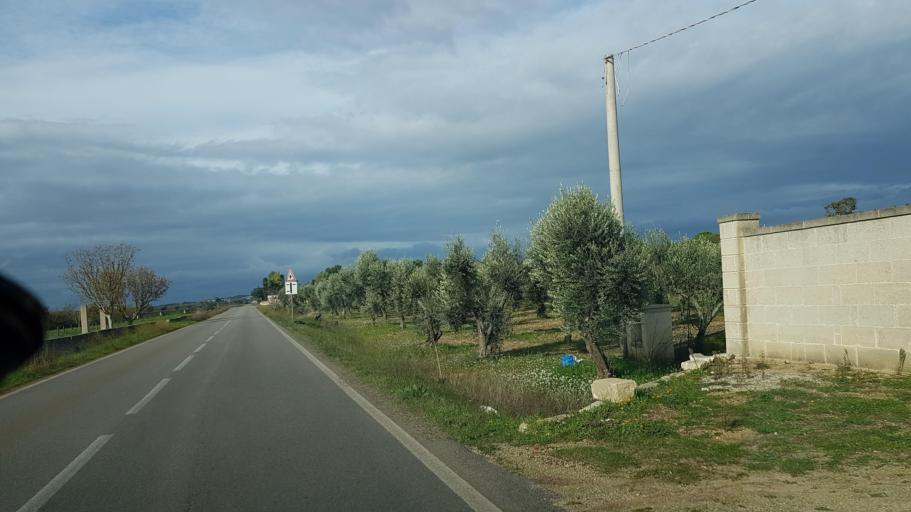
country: IT
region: Apulia
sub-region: Provincia di Brindisi
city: Torre Santa Susanna
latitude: 40.4778
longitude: 17.6960
